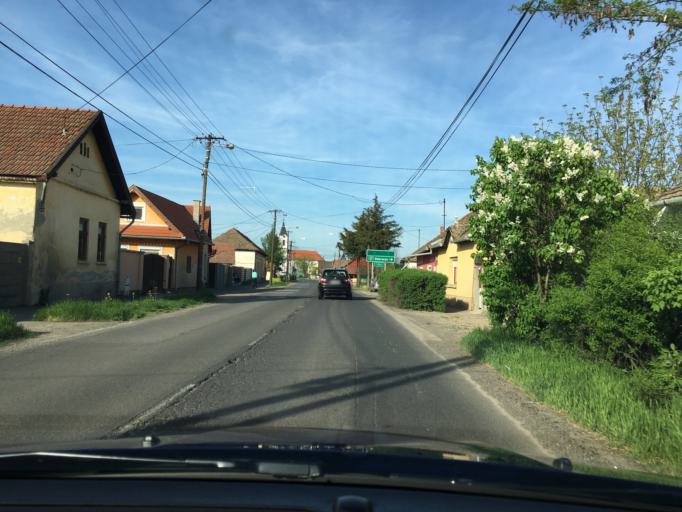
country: HU
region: Bekes
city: Mezobereny
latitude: 46.8150
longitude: 21.0200
